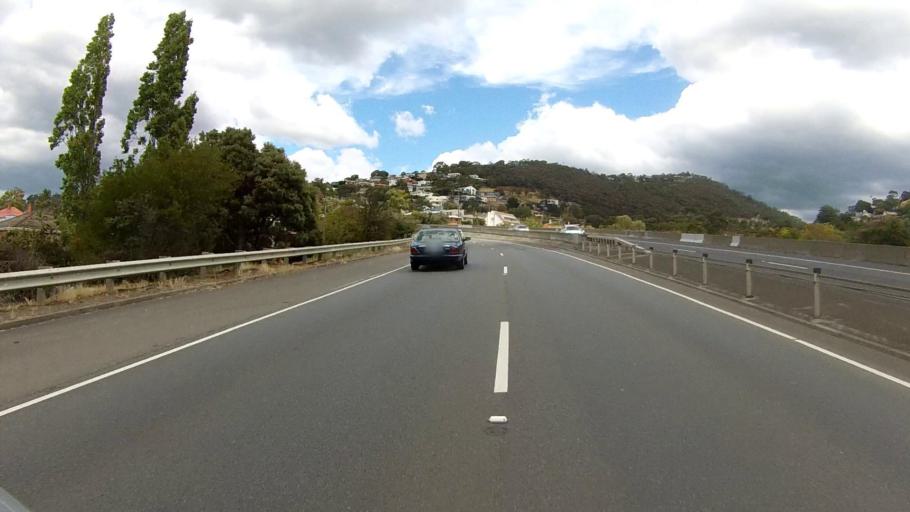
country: AU
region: Tasmania
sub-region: Hobart
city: Dynnyrne
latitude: -42.8987
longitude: 147.3159
